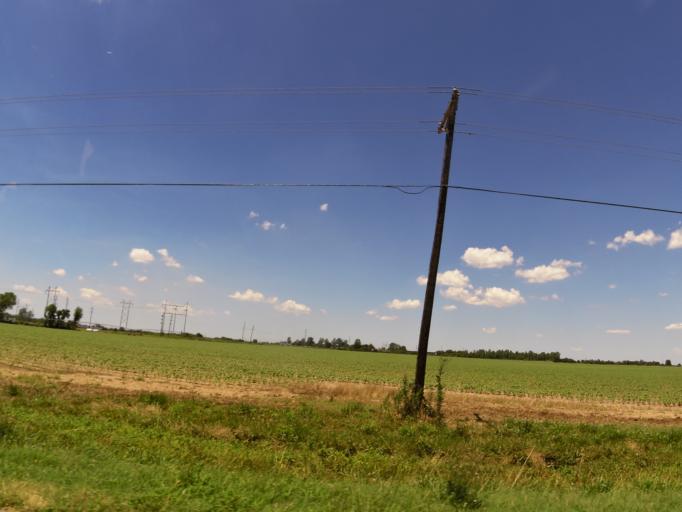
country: US
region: Missouri
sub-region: New Madrid County
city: New Madrid
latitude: 36.5765
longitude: -89.5650
